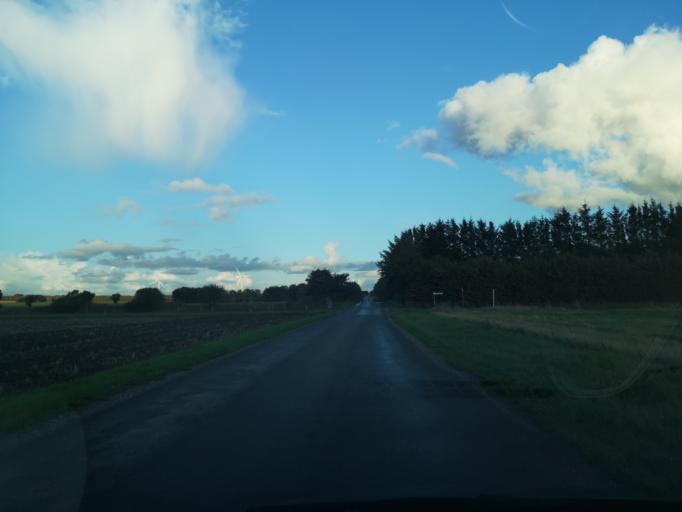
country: DK
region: Central Jutland
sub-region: Ringkobing-Skjern Kommune
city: Skjern
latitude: 56.0221
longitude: 8.5526
